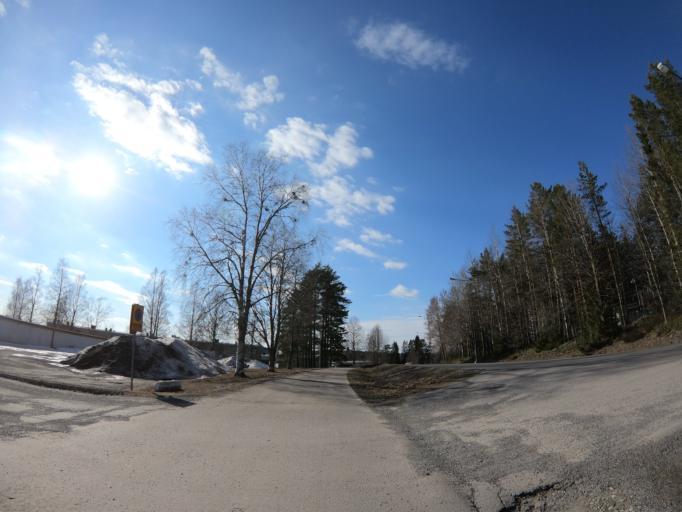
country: SE
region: Vaesterbotten
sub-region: Umea Kommun
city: Ersmark
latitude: 63.8379
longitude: 20.3260
